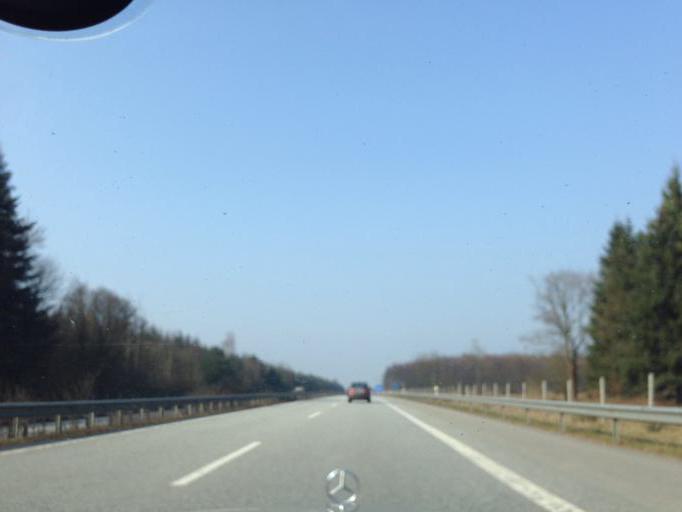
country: DE
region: Schleswig-Holstein
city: Daldorf
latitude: 54.0297
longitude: 10.2446
